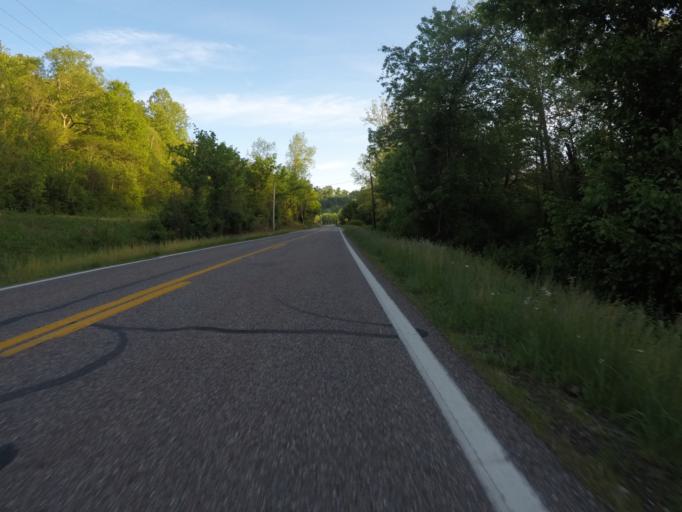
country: US
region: West Virginia
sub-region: Cabell County
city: Huntington
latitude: 38.4979
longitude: -82.4757
